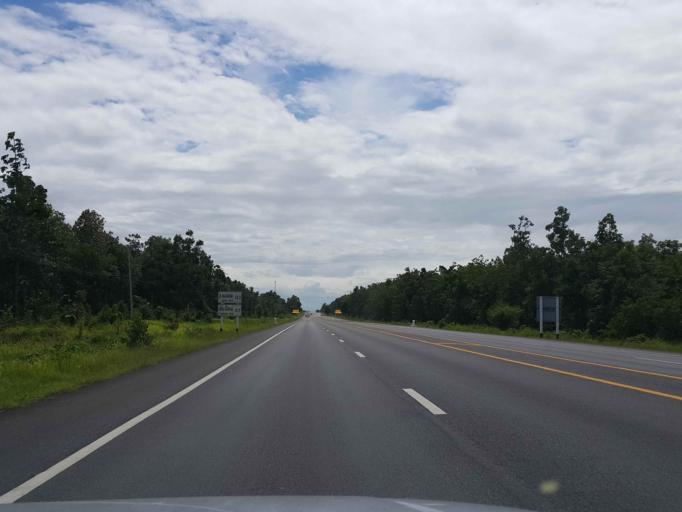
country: TH
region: Sukhothai
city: Ban Dan Lan Hoi
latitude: 16.9769
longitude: 99.4717
